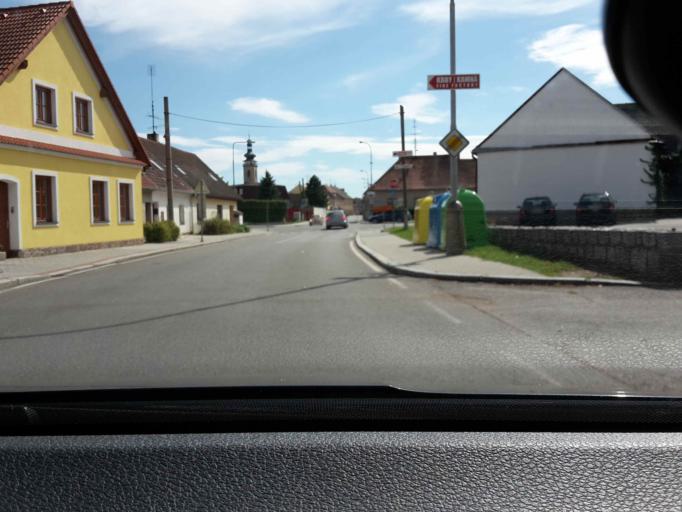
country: CZ
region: Jihocesky
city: Sobeslav
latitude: 49.2642
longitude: 14.7164
